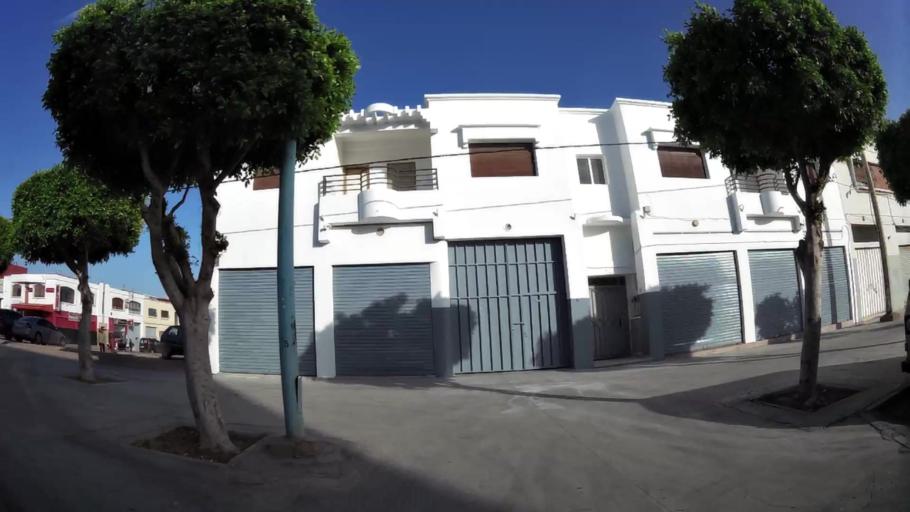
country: MA
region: Oued ed Dahab-Lagouira
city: Dakhla
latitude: 30.4117
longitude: -9.5466
